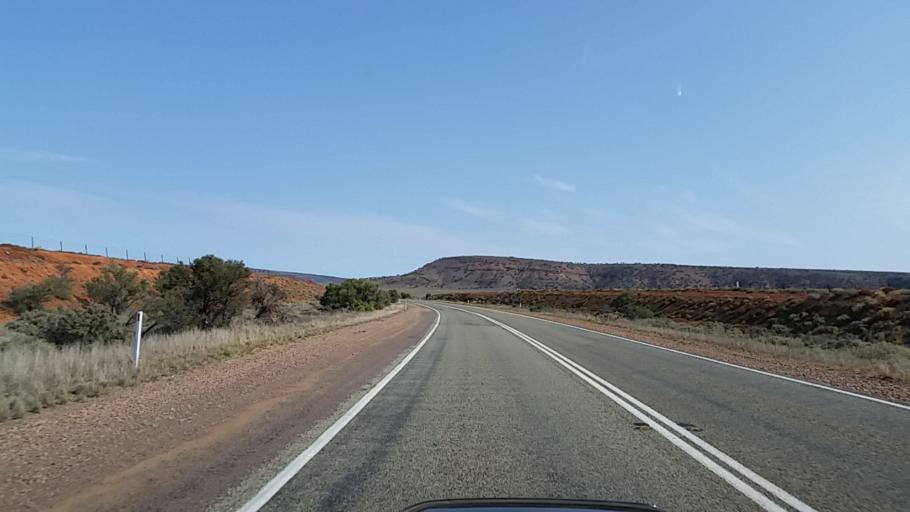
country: AU
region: South Australia
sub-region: Port Augusta
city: Port Augusta West
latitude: -32.5482
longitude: 137.6342
